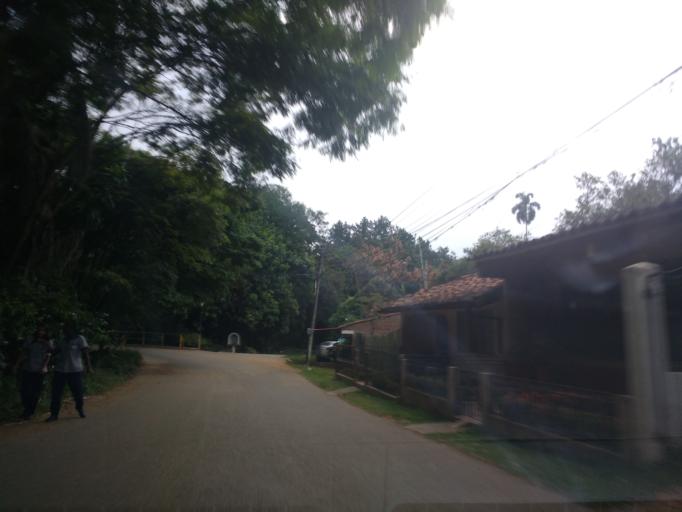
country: CO
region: Cauca
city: Santander de Quilichao
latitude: 3.0016
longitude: -76.4771
